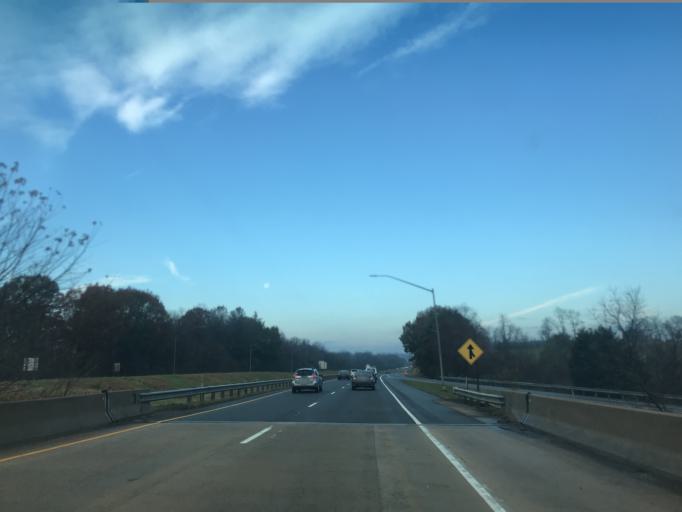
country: US
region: Maryland
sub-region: Washington County
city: Robinwood
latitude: 39.5866
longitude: -77.6411
